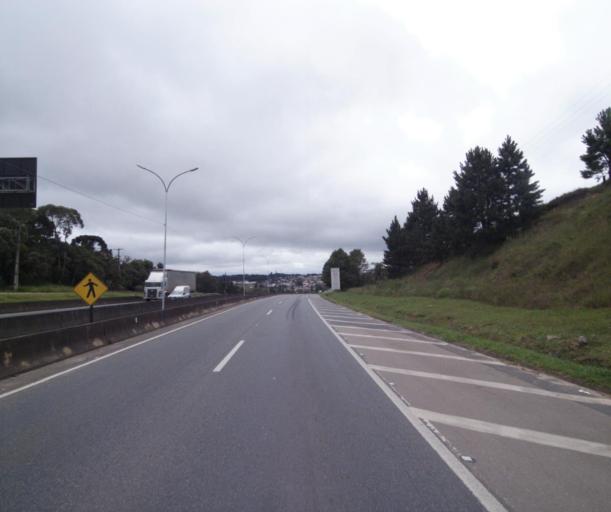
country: BR
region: Parana
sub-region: Quatro Barras
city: Quatro Barras
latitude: -25.3639
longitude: -49.0851
